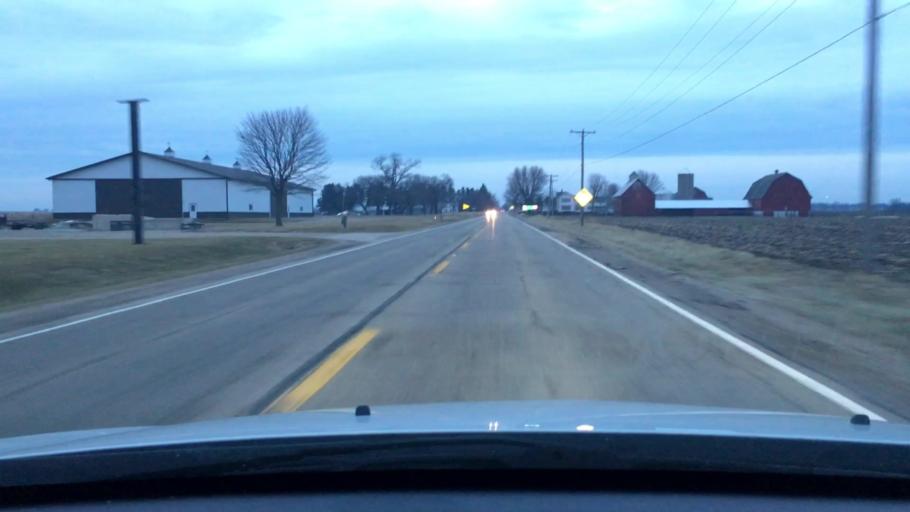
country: US
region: Illinois
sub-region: LaSalle County
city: Mendota
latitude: 41.5138
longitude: -89.1272
